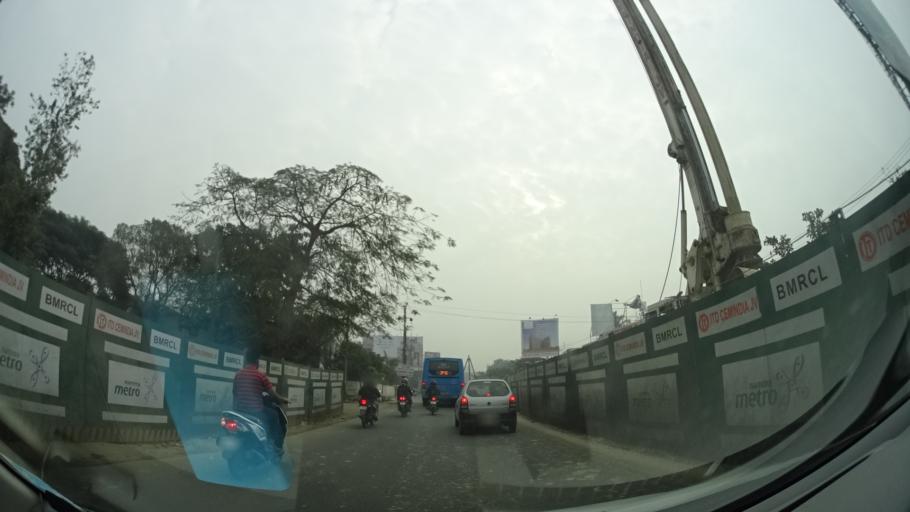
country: IN
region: Karnataka
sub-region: Bangalore Urban
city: Bangalore
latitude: 12.9968
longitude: 77.6923
